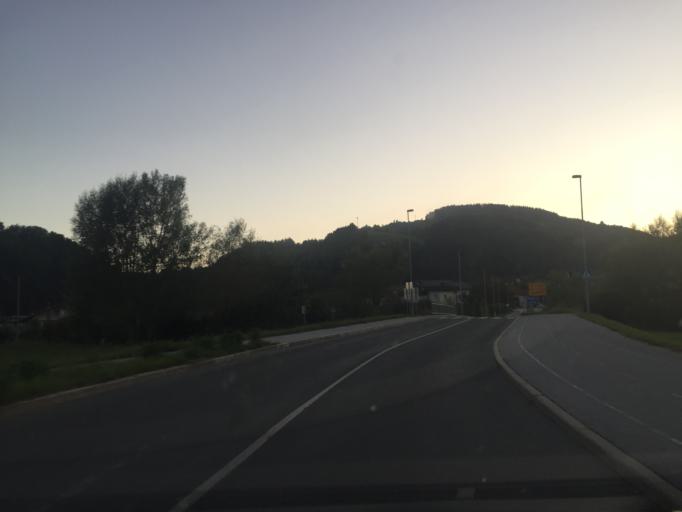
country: SI
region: Sostanj
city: Sostanj
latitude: 46.3845
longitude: 15.0342
